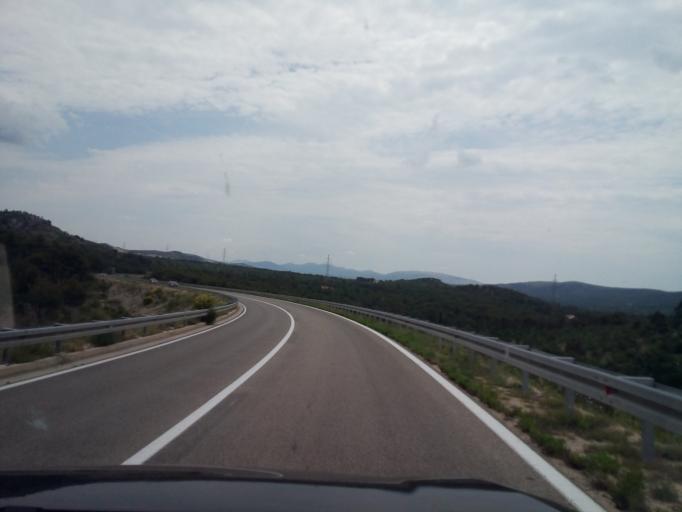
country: HR
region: Sibensko-Kniniska
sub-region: Grad Sibenik
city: Sibenik
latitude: 43.7518
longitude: 15.9369
